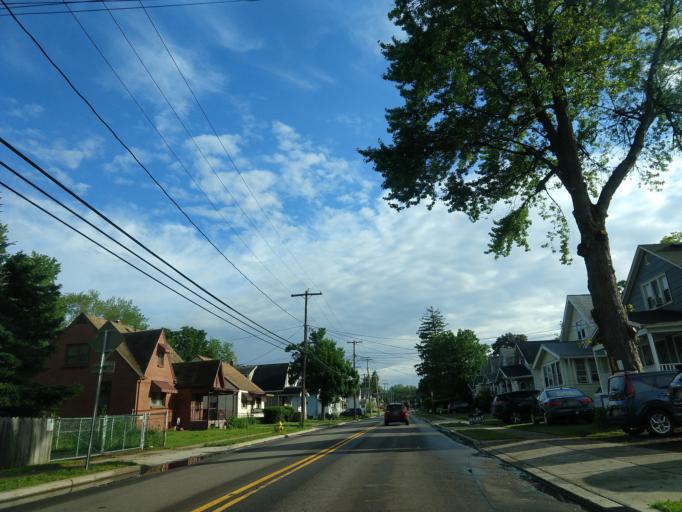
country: US
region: New York
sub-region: Erie County
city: West Seneca
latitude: 42.8468
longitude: -78.7884
